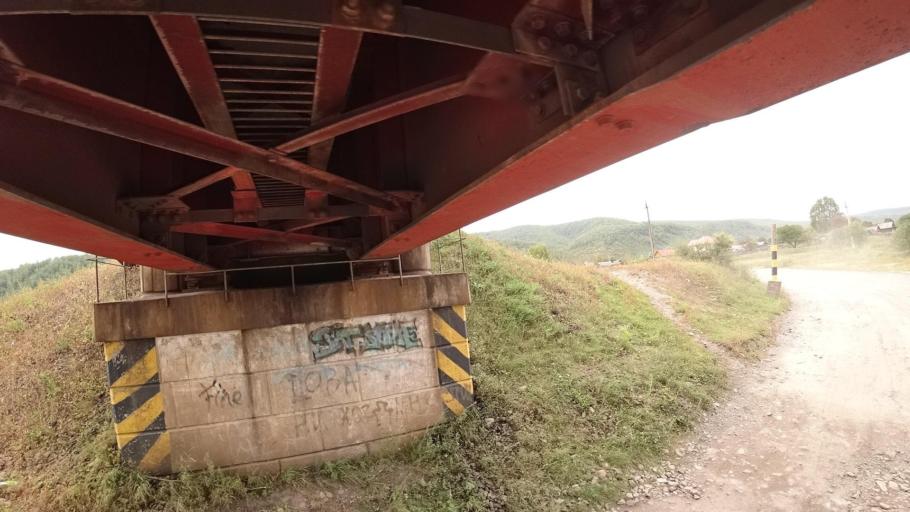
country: RU
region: Jewish Autonomous Oblast
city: Khingansk
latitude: 49.0303
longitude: 131.0507
